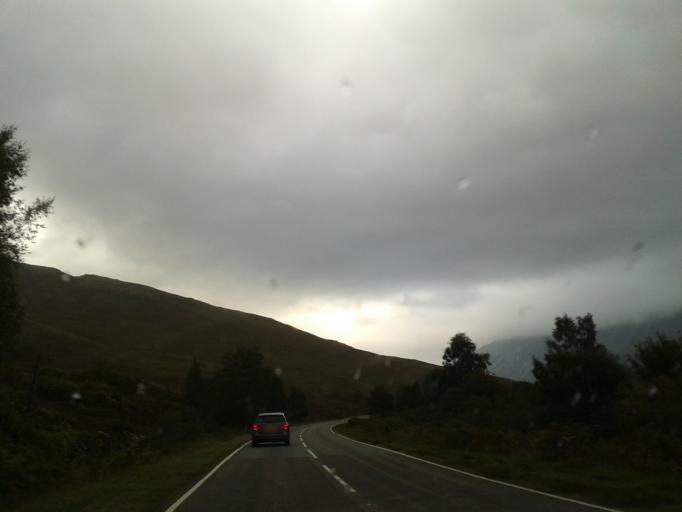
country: GB
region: Scotland
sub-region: Highland
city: Spean Bridge
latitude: 57.1473
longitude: -5.0989
